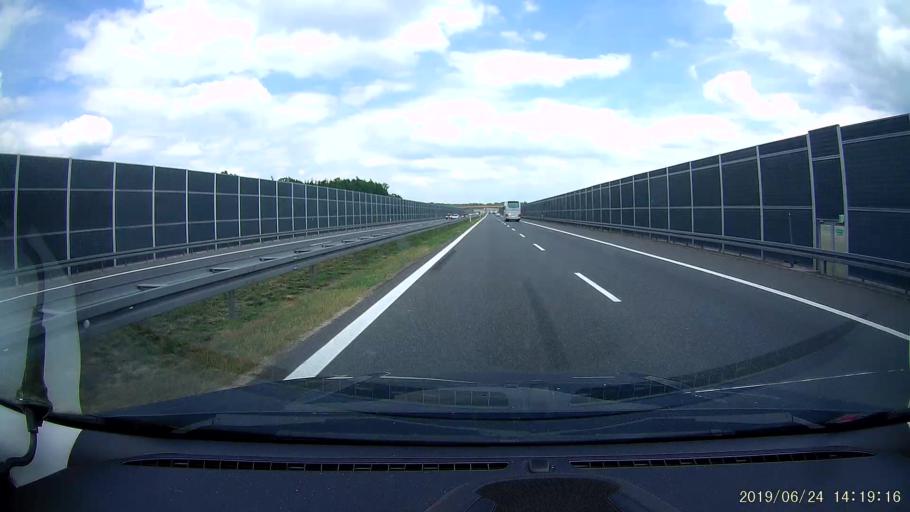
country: PL
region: Lesser Poland Voivodeship
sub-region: Powiat bochenski
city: Lapczyca
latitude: 49.9998
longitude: 20.3960
